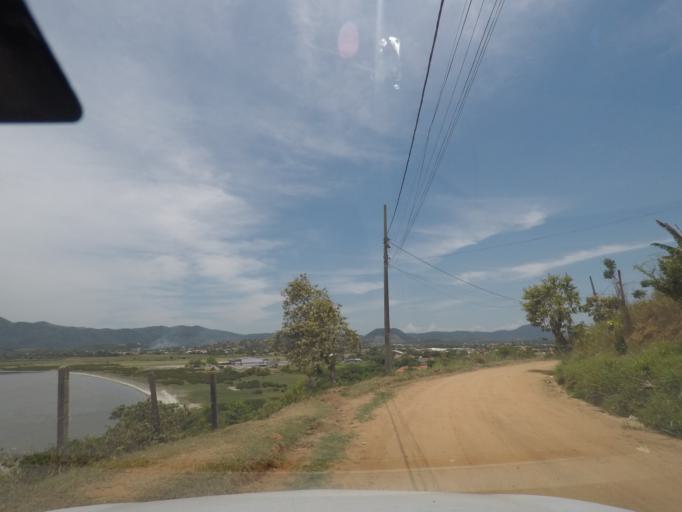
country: BR
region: Rio de Janeiro
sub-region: Marica
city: Marica
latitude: -22.9250
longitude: -42.8274
